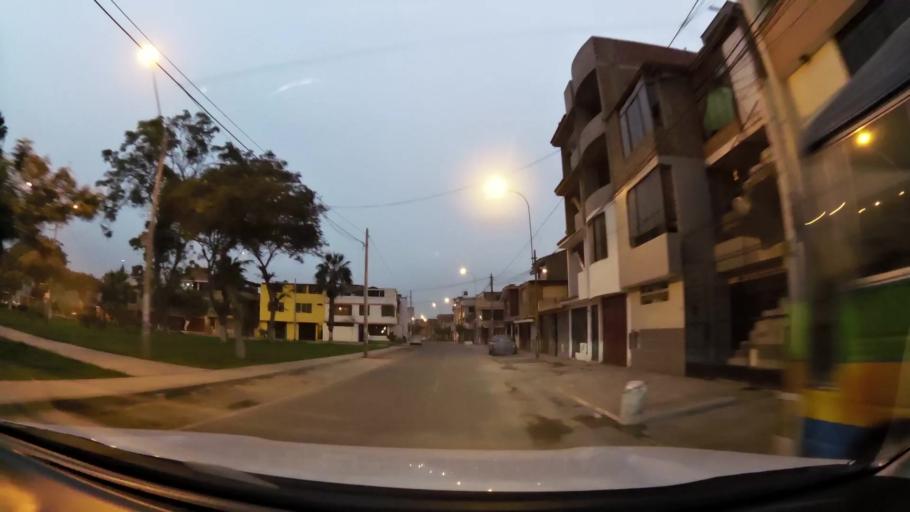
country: PE
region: Lima
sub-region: Lima
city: Surco
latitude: -12.1637
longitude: -76.9681
